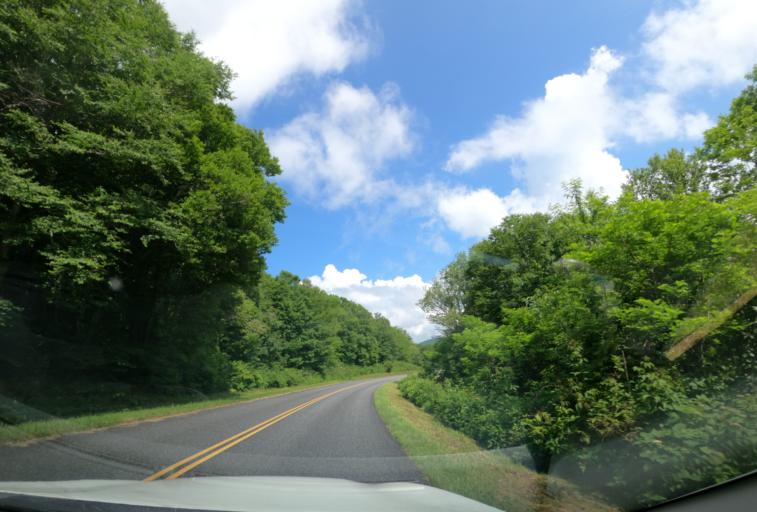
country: US
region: North Carolina
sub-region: Haywood County
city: Hazelwood
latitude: 35.3964
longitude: -83.0422
